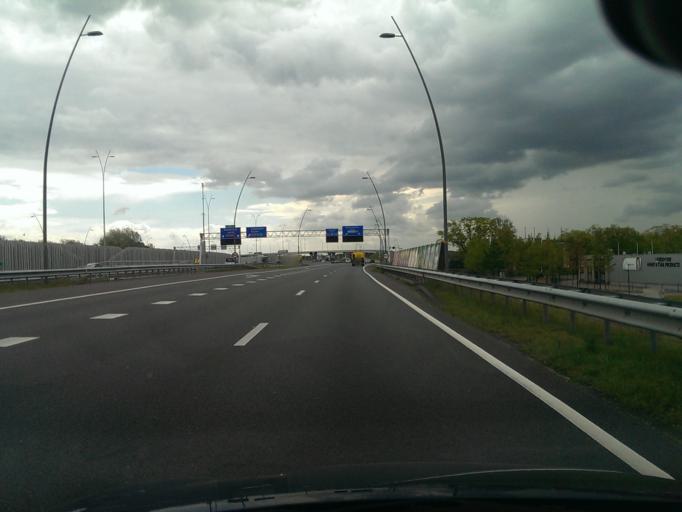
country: NL
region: North Brabant
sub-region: Gemeente Veldhoven
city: Veldhoven
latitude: 51.4119
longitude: 5.4295
